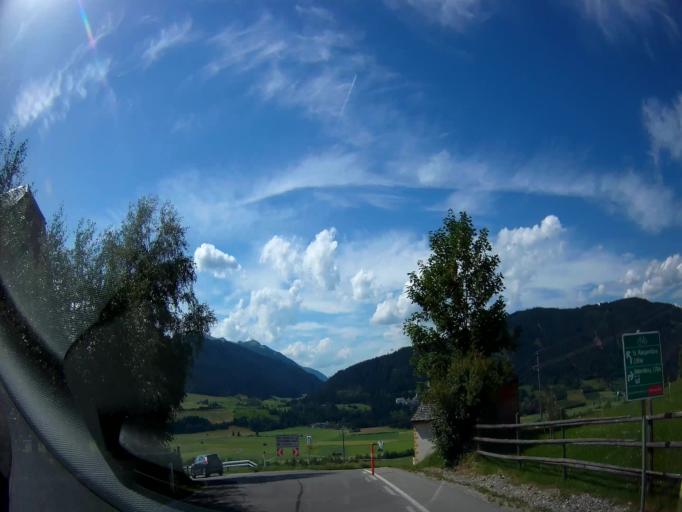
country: AT
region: Salzburg
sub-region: Politischer Bezirk Tamsweg
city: Thomatal
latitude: 47.0851
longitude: 13.7194
